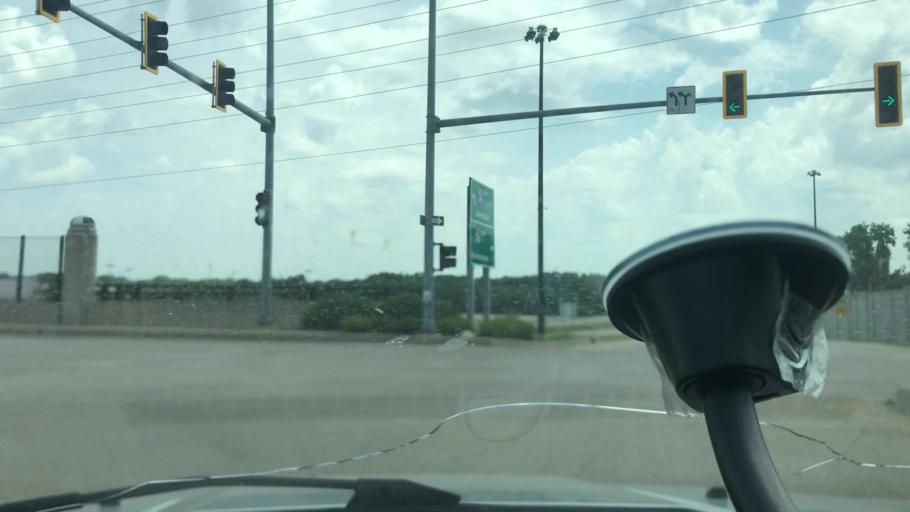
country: US
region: Illinois
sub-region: Peoria County
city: West Peoria
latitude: 40.7374
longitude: -89.6317
